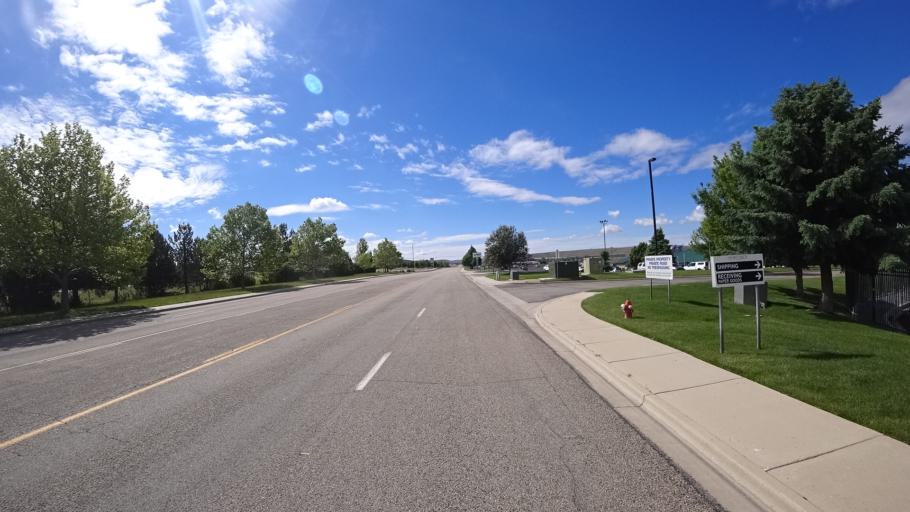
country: US
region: Idaho
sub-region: Ada County
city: Boise
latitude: 43.5371
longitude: -116.1620
